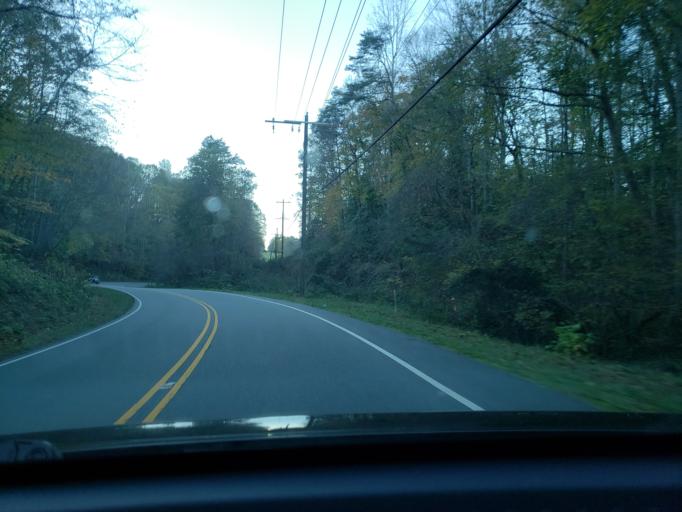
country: US
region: North Carolina
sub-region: Stokes County
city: Danbury
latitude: 36.3863
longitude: -80.1895
